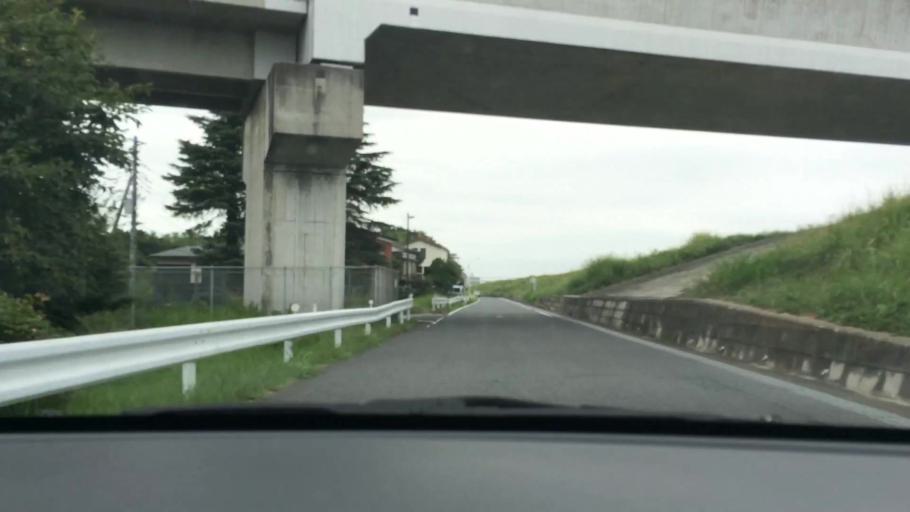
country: JP
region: Chiba
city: Nagareyama
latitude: 35.8307
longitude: 139.8859
